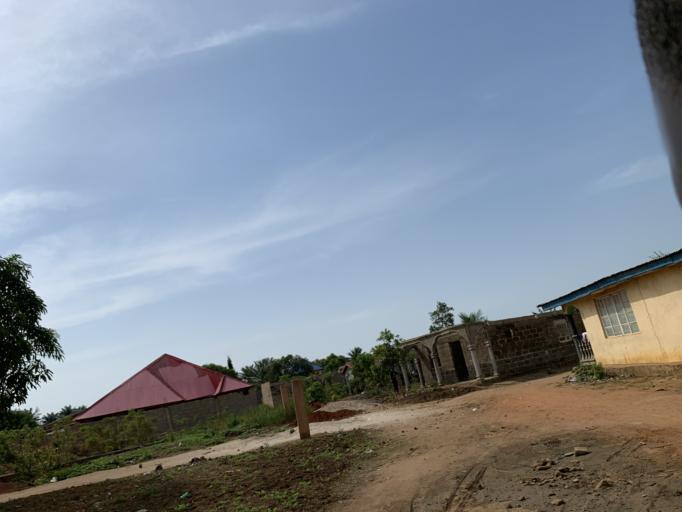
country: SL
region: Western Area
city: Waterloo
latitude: 8.3463
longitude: -13.0392
